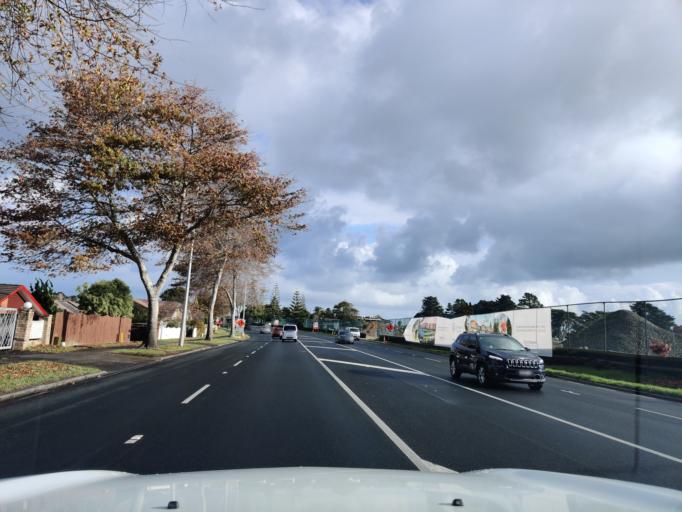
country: NZ
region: Auckland
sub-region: Auckland
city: Pakuranga
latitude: -36.9172
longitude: 174.9140
